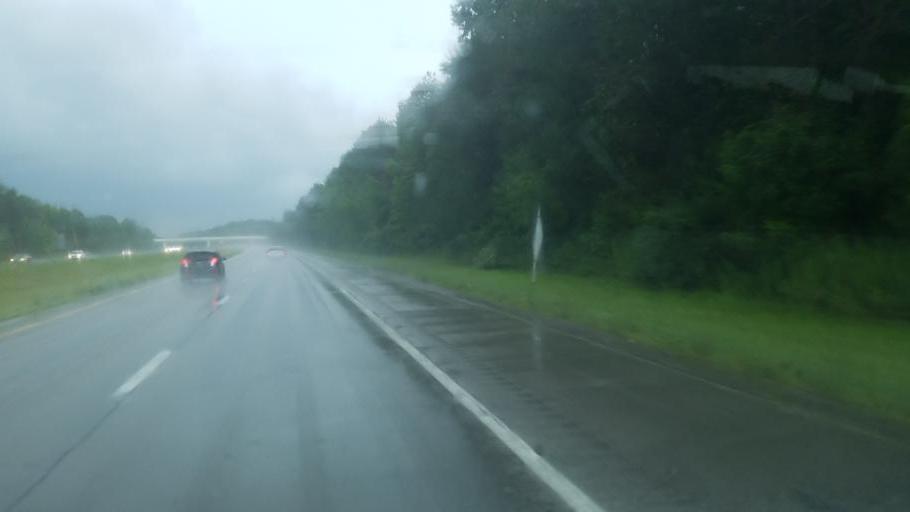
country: US
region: Ohio
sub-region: Trumbull County
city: McKinley Heights
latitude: 41.2098
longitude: -80.7104
